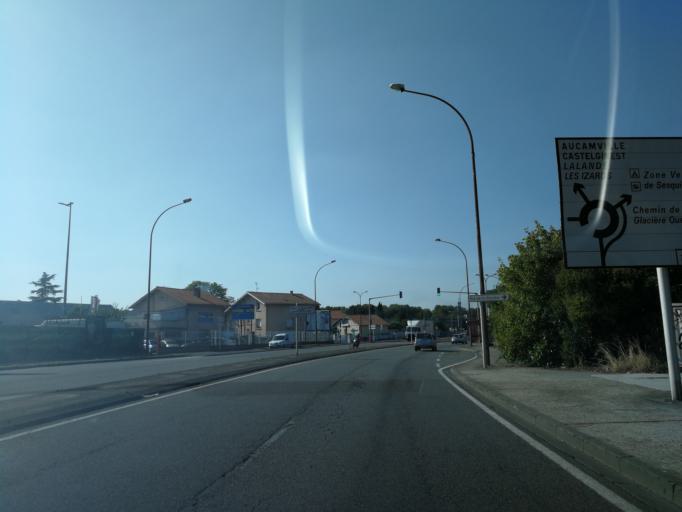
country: FR
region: Midi-Pyrenees
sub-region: Departement de la Haute-Garonne
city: Aucamville
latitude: 43.6459
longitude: 1.4265
